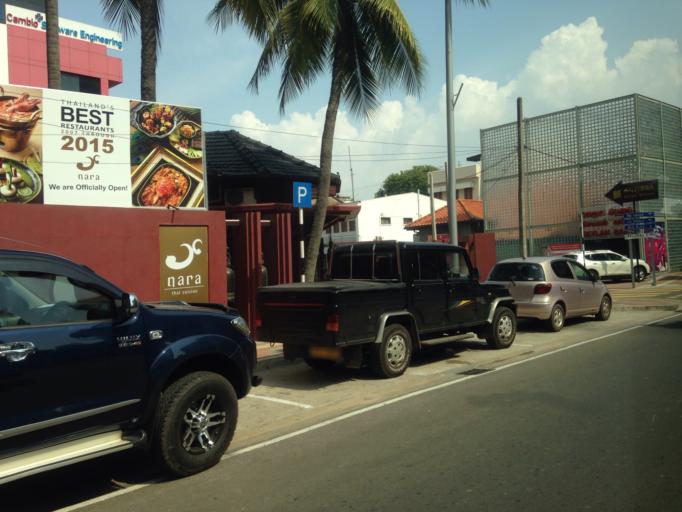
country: LK
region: Western
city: Colombo
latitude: 6.9071
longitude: 79.8533
